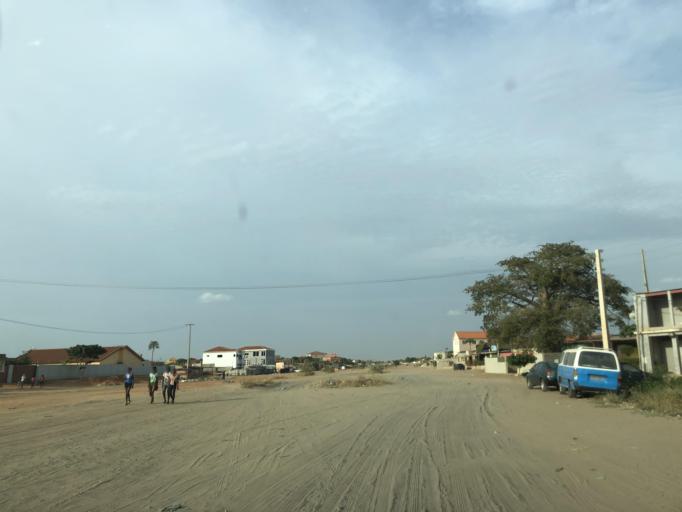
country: AO
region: Luanda
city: Luanda
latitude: -8.9267
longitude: 13.3043
